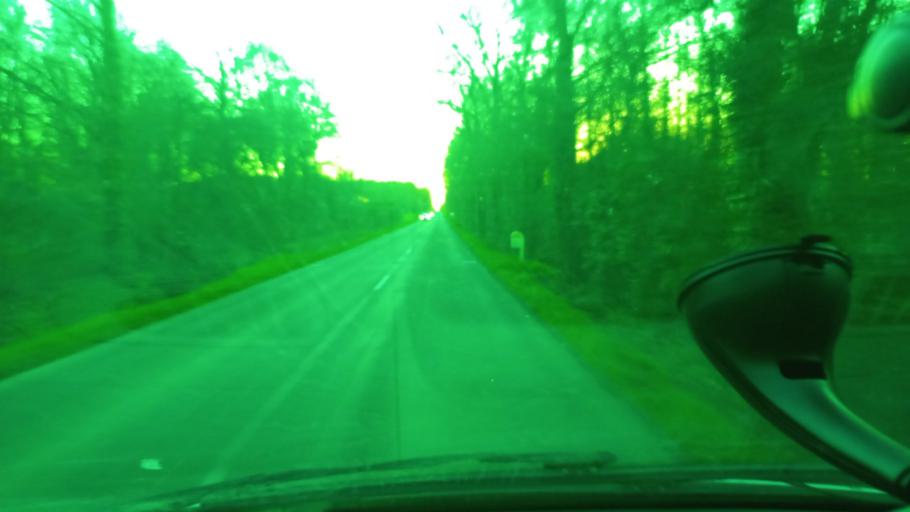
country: FR
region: Pays de la Loire
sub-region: Departement de la Vendee
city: Saint-Denis-la-Chevasse
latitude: 46.8040
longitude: -1.3859
